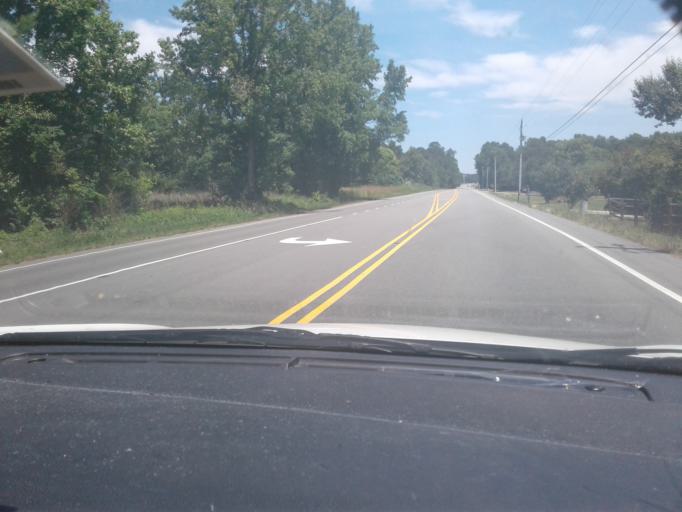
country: US
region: North Carolina
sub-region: Harnett County
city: Lillington
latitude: 35.4661
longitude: -78.8284
